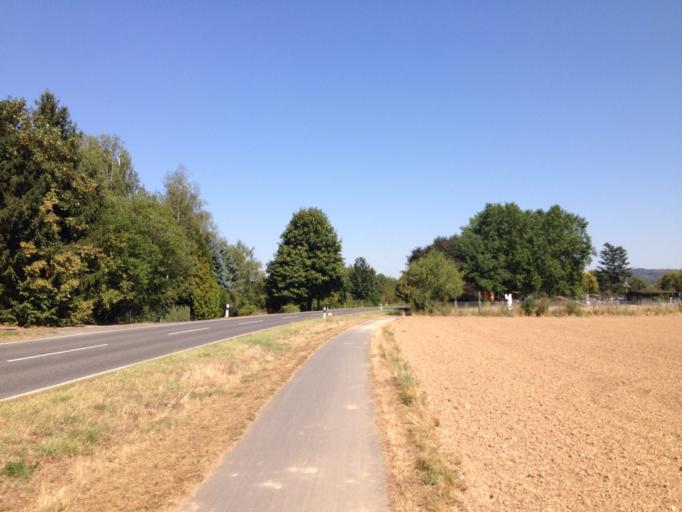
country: DE
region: Hesse
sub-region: Regierungsbezirk Giessen
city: Giessen
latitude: 50.6134
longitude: 8.6815
